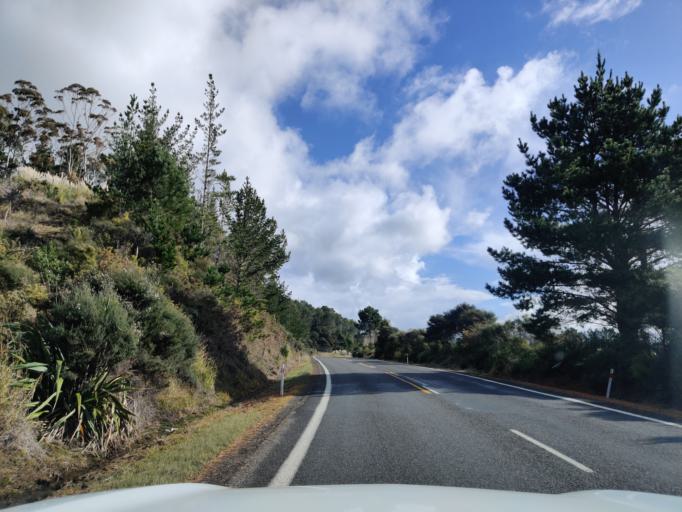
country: NZ
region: Waikato
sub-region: Thames-Coromandel District
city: Whitianga
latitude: -36.7483
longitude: 175.6741
